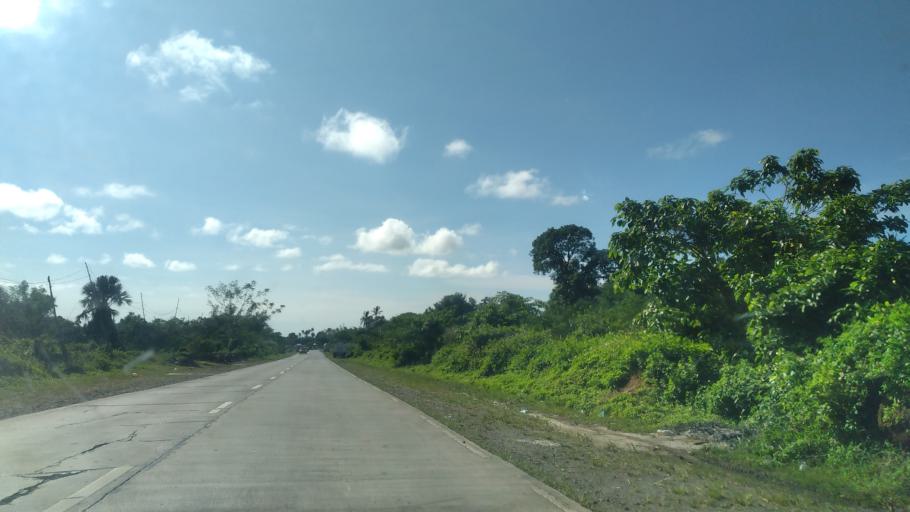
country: PH
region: Calabarzon
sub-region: Province of Quezon
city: Isabang
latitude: 13.9592
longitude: 121.5779
